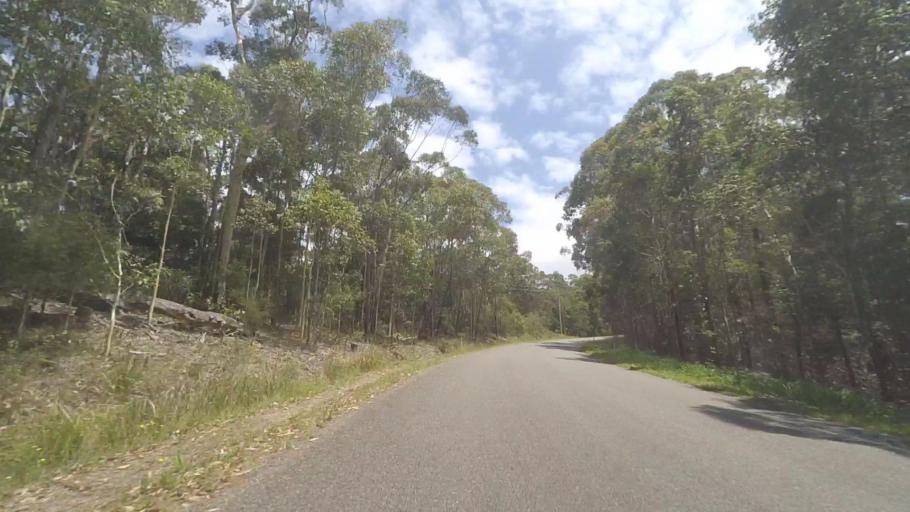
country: AU
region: New South Wales
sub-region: Shoalhaven Shire
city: Milton
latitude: -35.4019
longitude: 150.3646
